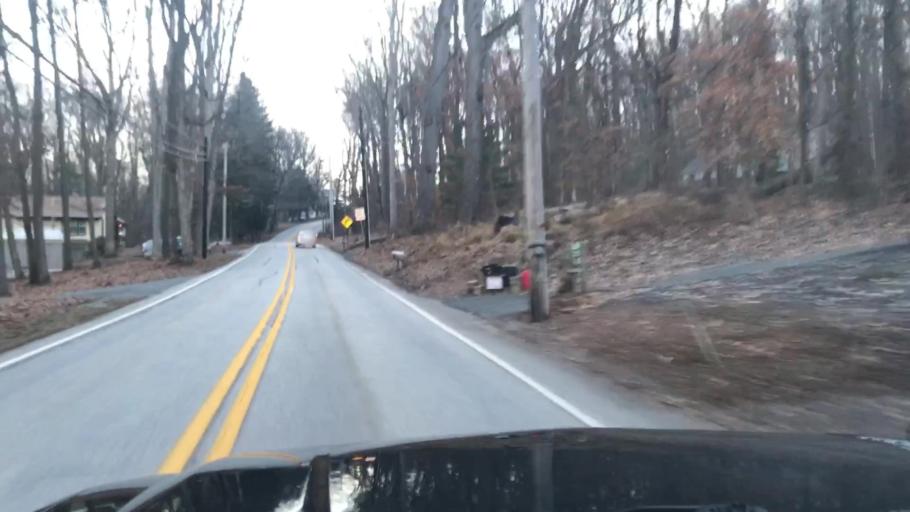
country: US
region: Pennsylvania
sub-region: Cumberland County
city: Lower Allen
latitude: 40.1767
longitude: -76.8874
